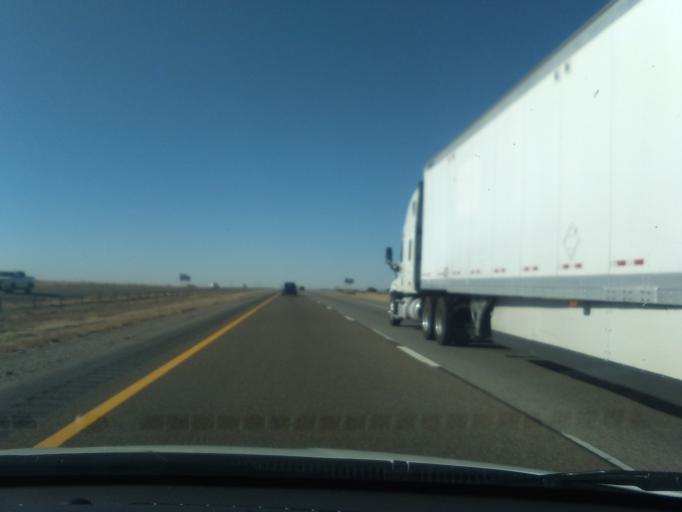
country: US
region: New Mexico
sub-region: Sandoval County
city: Santo Domingo Pueblo
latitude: 35.4520
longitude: -106.3492
